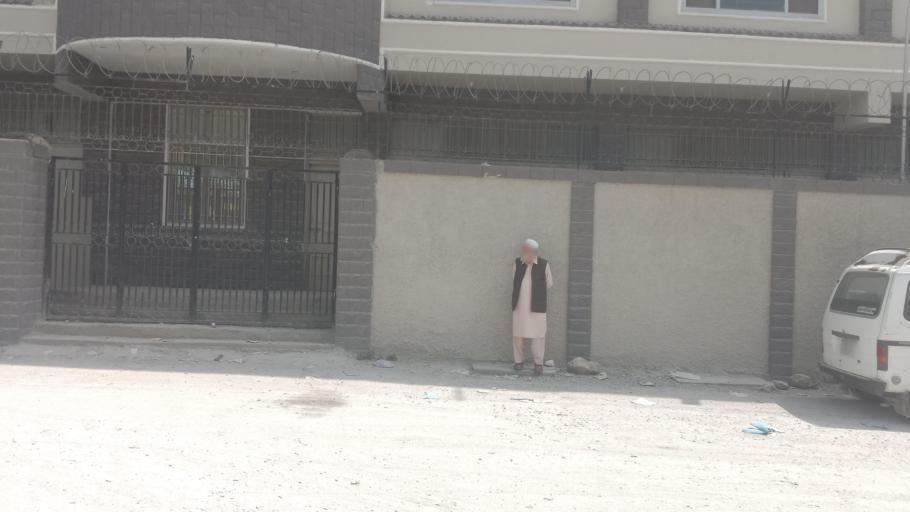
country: PK
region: Khyber Pakhtunkhwa
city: Abbottabad
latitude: 34.1561
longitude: 73.2662
